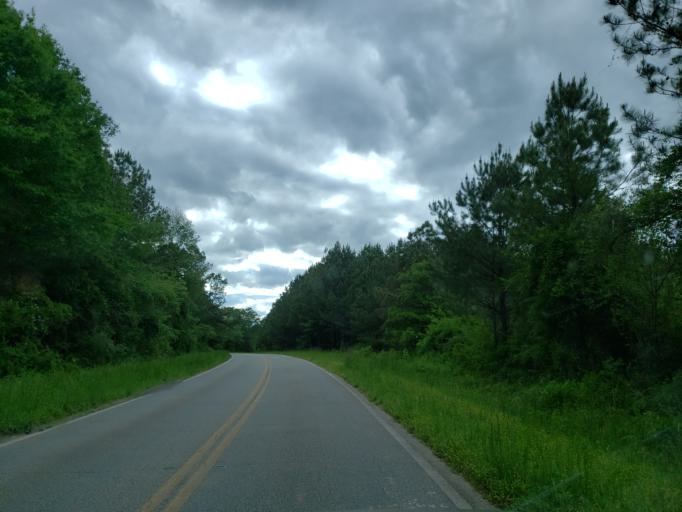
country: US
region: Georgia
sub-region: Haralson County
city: Tallapoosa
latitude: 33.7664
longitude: -85.3297
